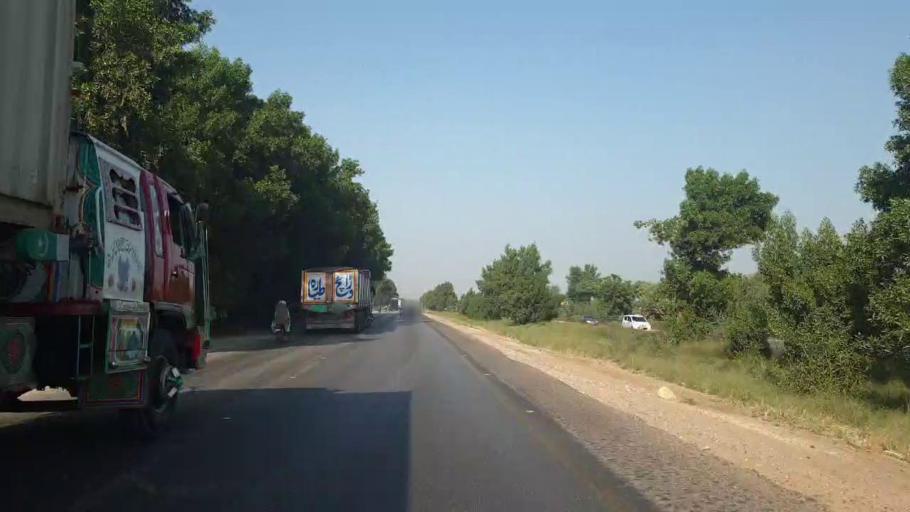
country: PK
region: Sindh
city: Matiari
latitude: 25.4943
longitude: 68.4231
